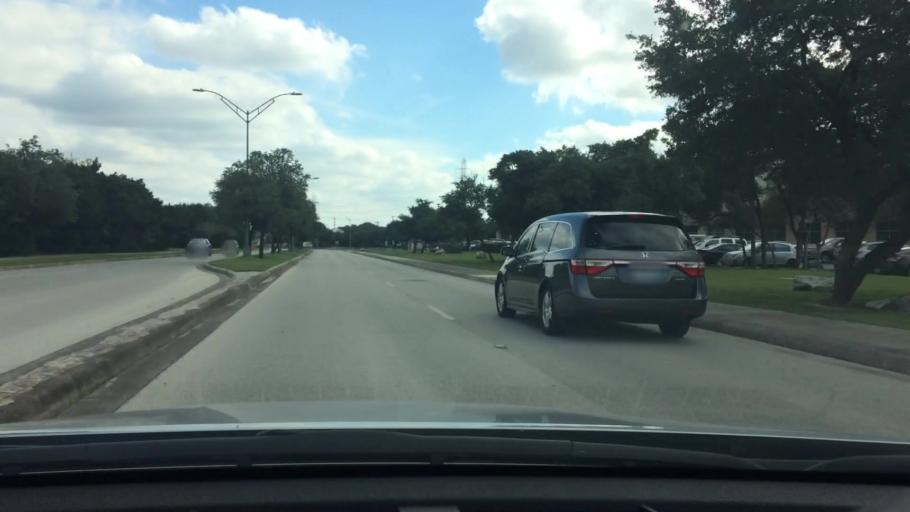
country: US
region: Texas
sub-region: Bexar County
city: Shavano Park
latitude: 29.5881
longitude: -98.5725
